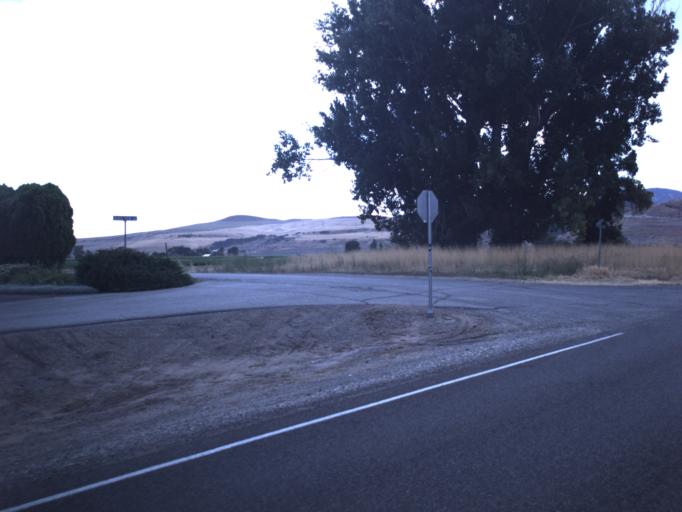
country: US
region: Utah
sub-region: Cache County
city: Lewiston
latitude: 41.9754
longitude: -111.9439
